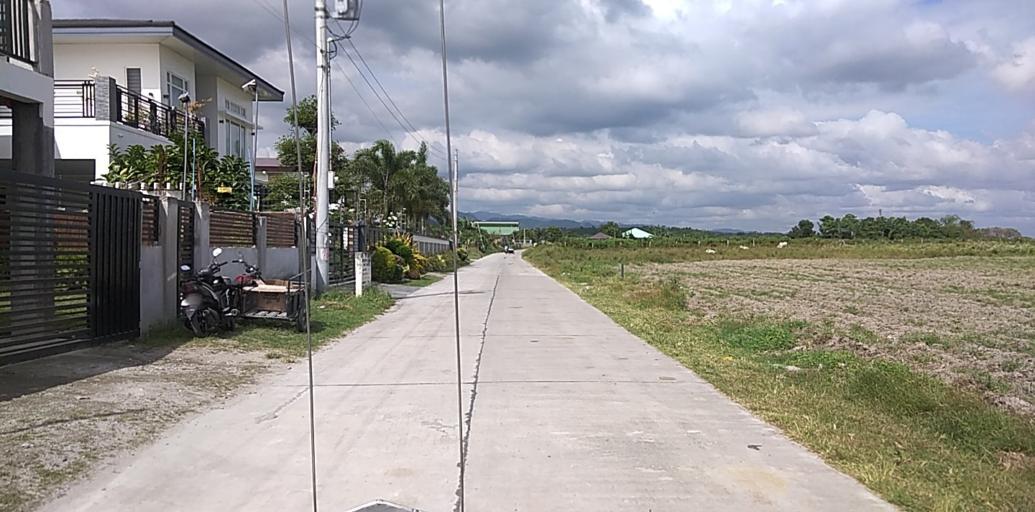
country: PH
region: Central Luzon
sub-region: Province of Pampanga
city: Porac
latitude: 15.0603
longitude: 120.5380
